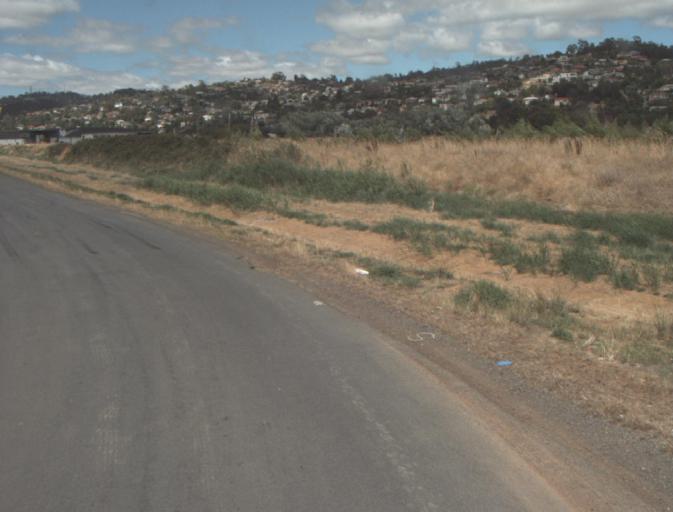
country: AU
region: Tasmania
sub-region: Launceston
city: Launceston
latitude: -41.4207
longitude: 147.1217
